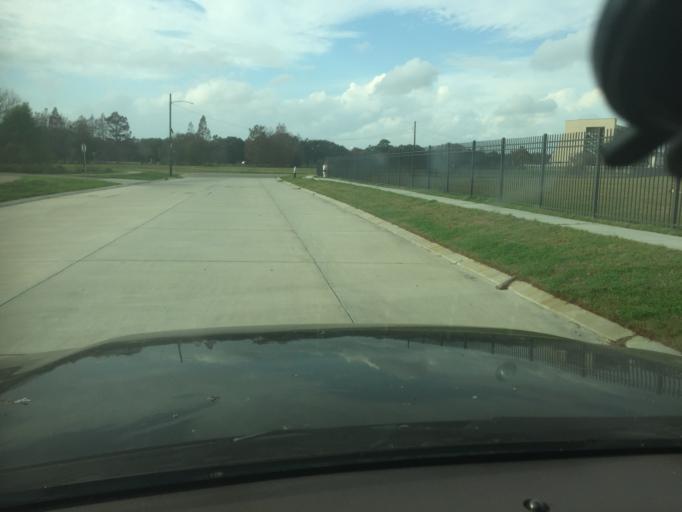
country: US
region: Louisiana
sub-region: Orleans Parish
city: New Orleans
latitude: 29.9960
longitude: -90.0837
